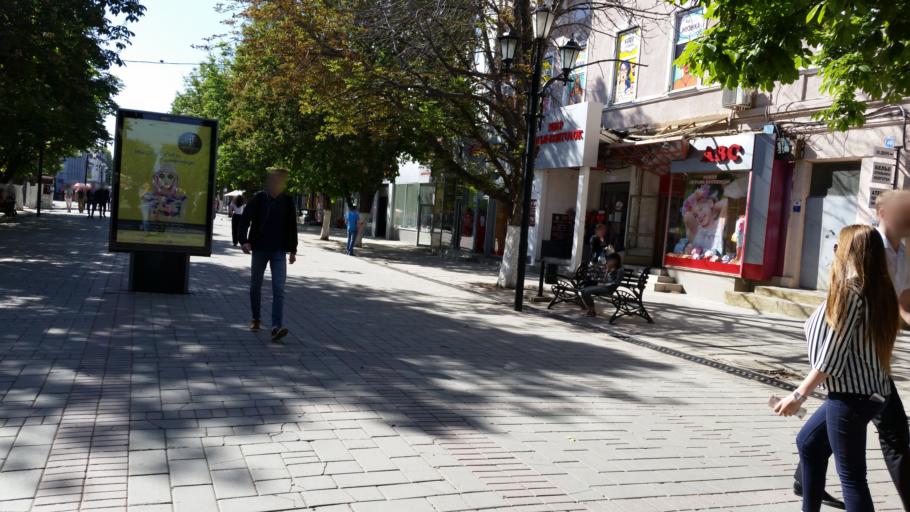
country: RU
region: Saratov
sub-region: Saratovskiy Rayon
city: Saratov
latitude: 51.5323
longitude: 46.0241
